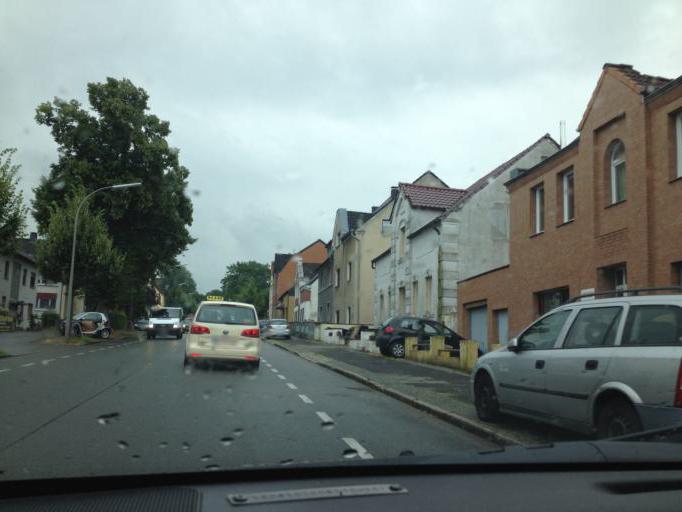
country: DE
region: North Rhine-Westphalia
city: Schwerte
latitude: 51.4801
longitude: 7.5277
